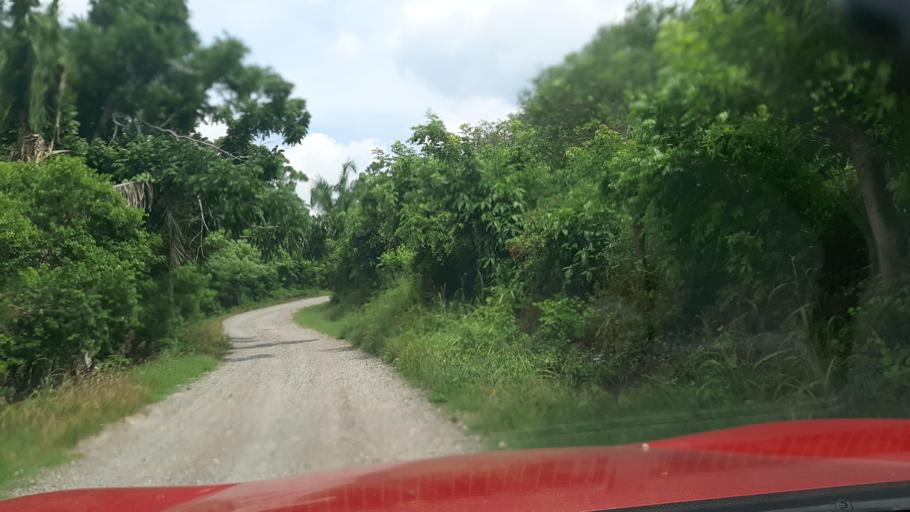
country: MX
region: Veracruz
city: Gutierrez Zamora
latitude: 20.4503
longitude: -97.1769
